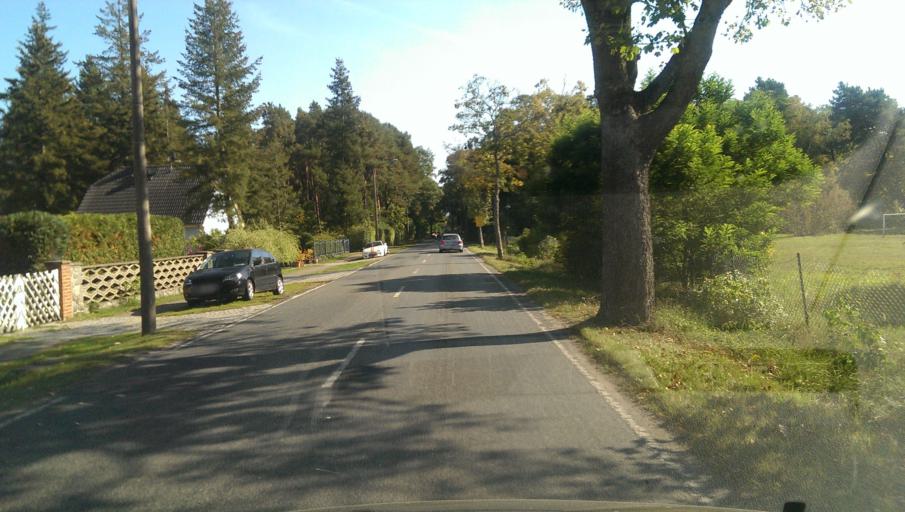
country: DE
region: Brandenburg
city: Teupitz
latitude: 52.1303
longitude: 13.6235
